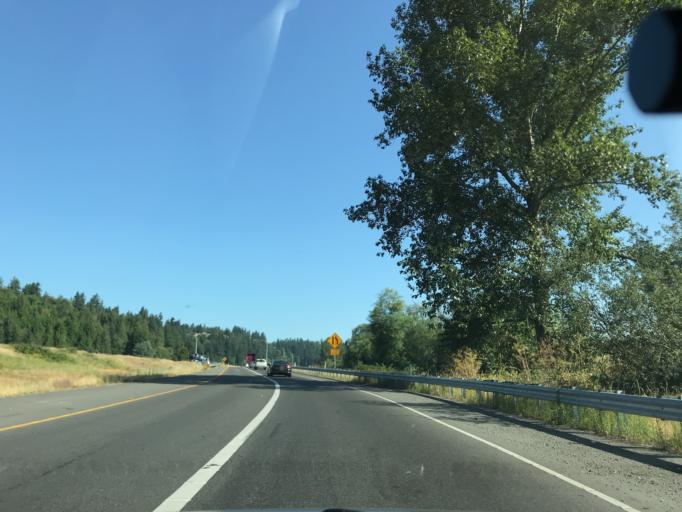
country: US
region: Washington
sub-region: King County
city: Pacific
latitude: 47.2506
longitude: -122.2562
